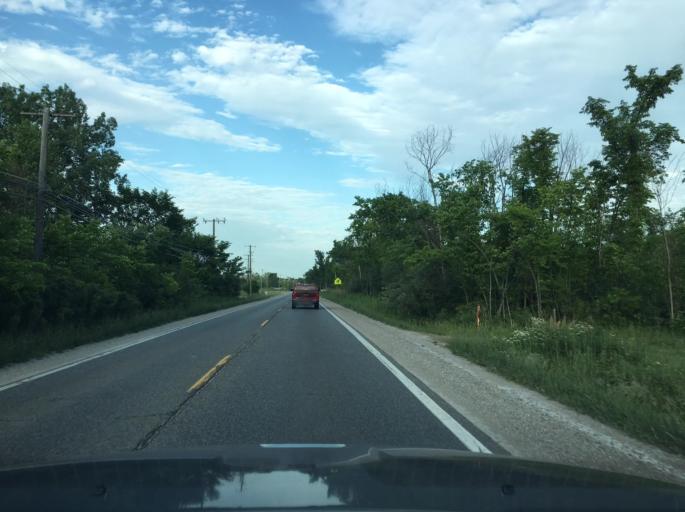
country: US
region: Michigan
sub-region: Macomb County
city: New Haven
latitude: 42.7174
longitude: -82.8925
